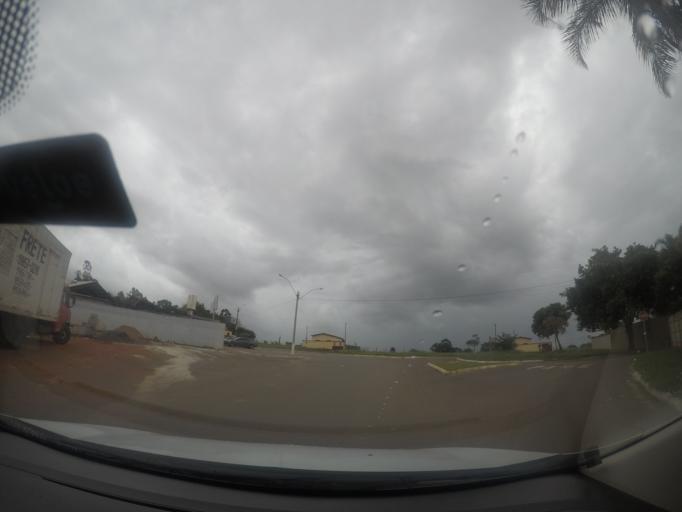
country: BR
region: Goias
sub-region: Trindade
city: Trindade
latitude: -16.6178
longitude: -49.3890
